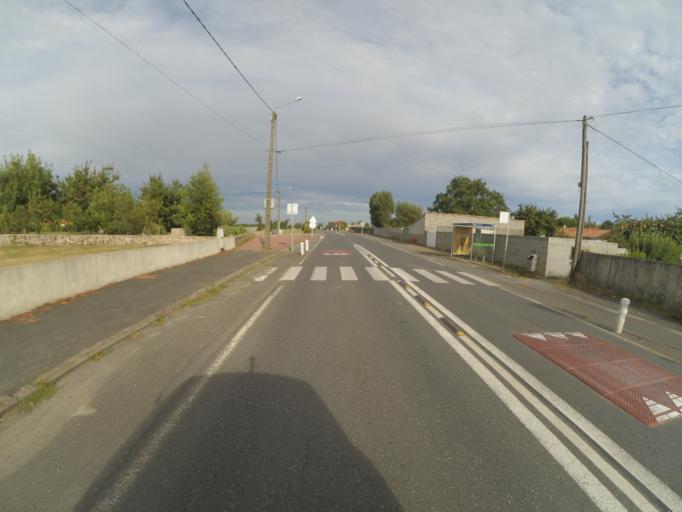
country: FR
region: Poitou-Charentes
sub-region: Departement des Deux-Sevres
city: Saint-Amand-sur-Sevre
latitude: 46.9283
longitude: -0.8106
